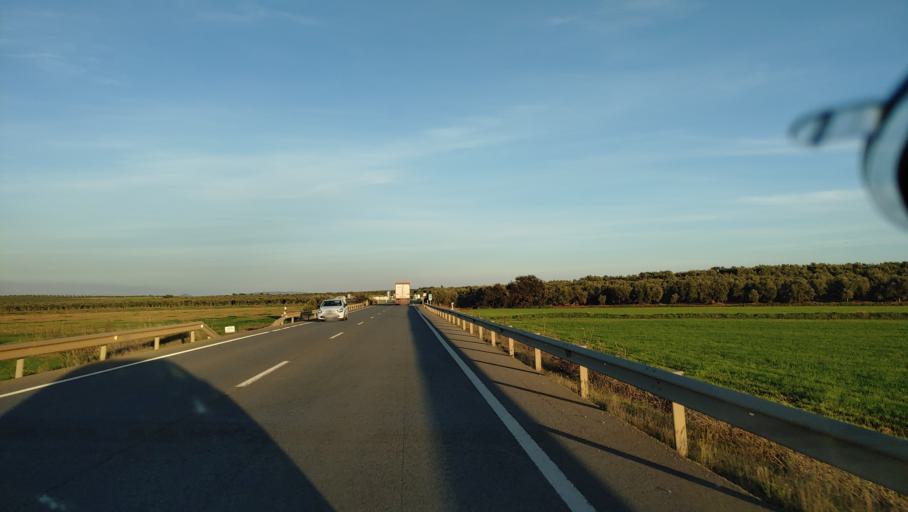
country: ES
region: Andalusia
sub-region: Provincia de Malaga
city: Campillos
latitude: 37.0483
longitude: -4.8286
